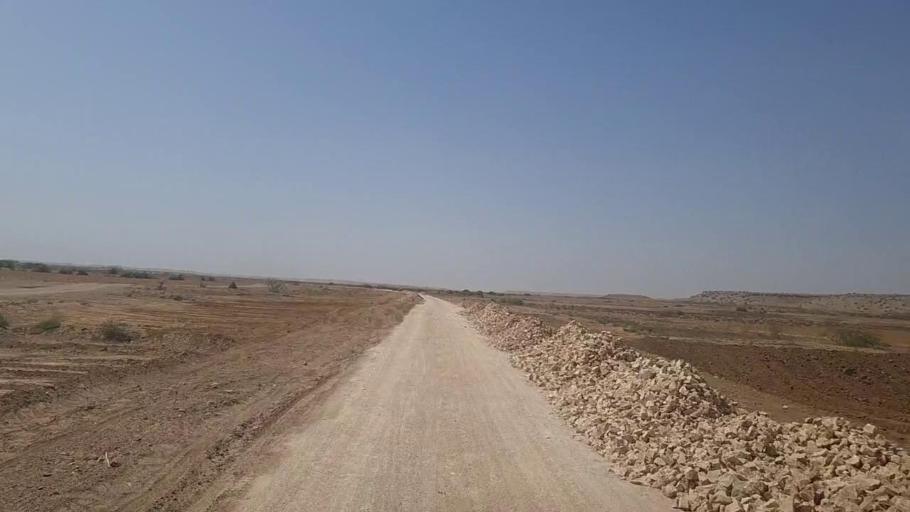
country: PK
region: Sindh
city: Kotri
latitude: 25.1477
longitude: 68.1748
